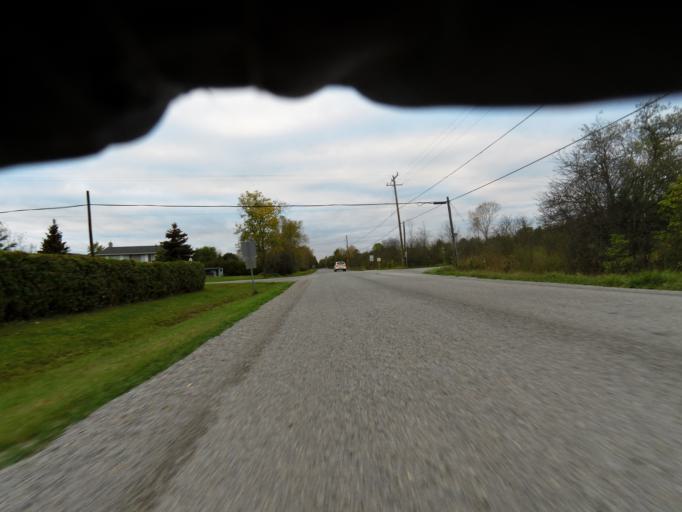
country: CA
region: Ontario
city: Quinte West
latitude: 44.0119
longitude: -77.7552
